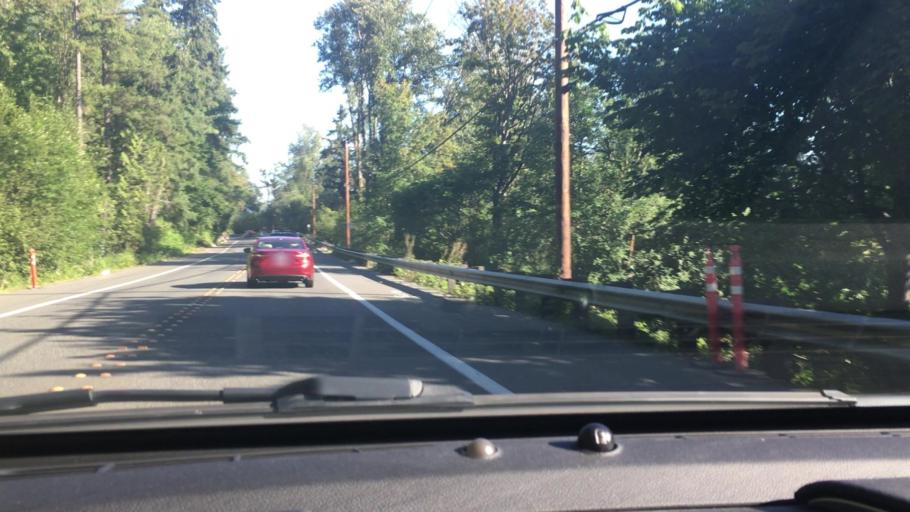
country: US
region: Washington
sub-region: King County
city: Sammamish
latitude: 47.6584
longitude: -122.0949
